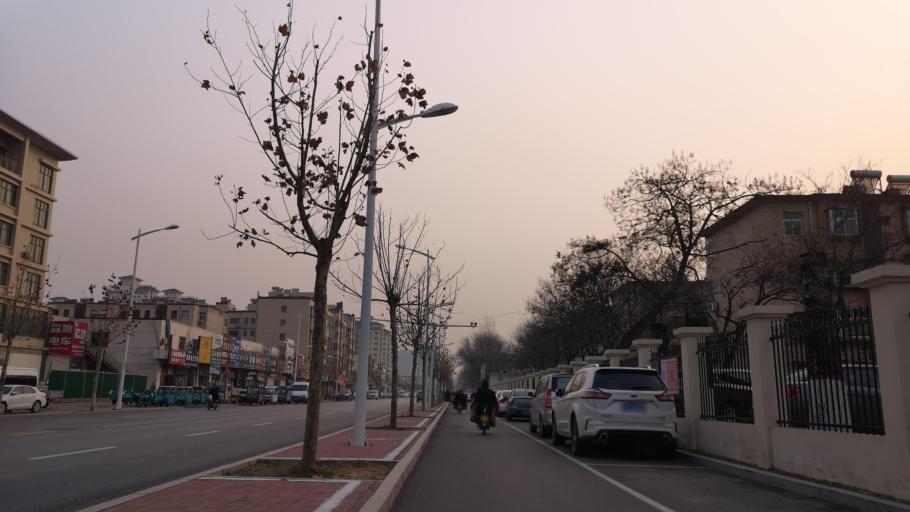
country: CN
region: Henan Sheng
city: Zhongyuanlu
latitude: 35.7886
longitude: 115.0821
